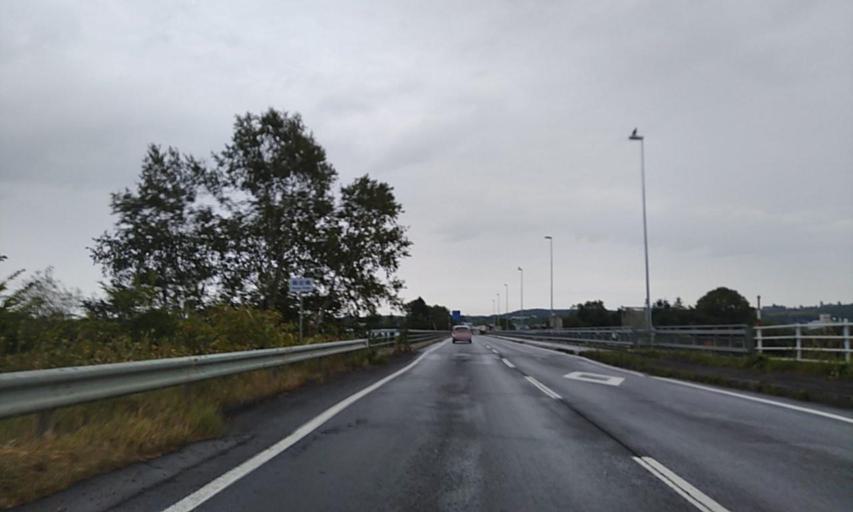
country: JP
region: Hokkaido
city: Mombetsu
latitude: 44.4760
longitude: 143.1163
